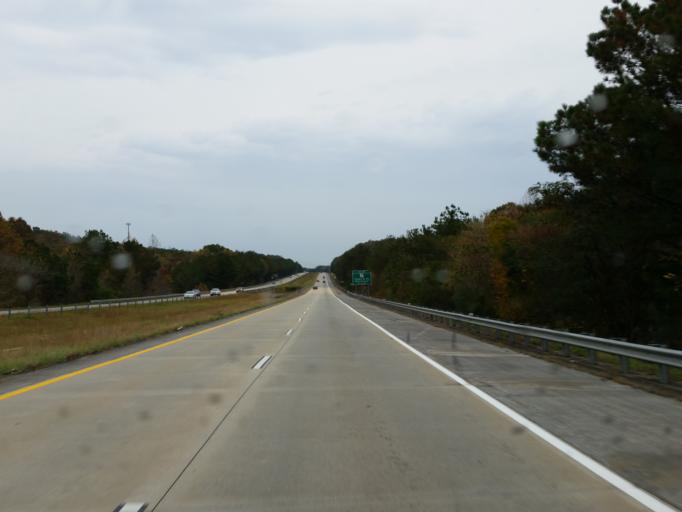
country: US
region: Georgia
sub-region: Cherokee County
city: Ball Ground
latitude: 34.3115
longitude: -84.4107
